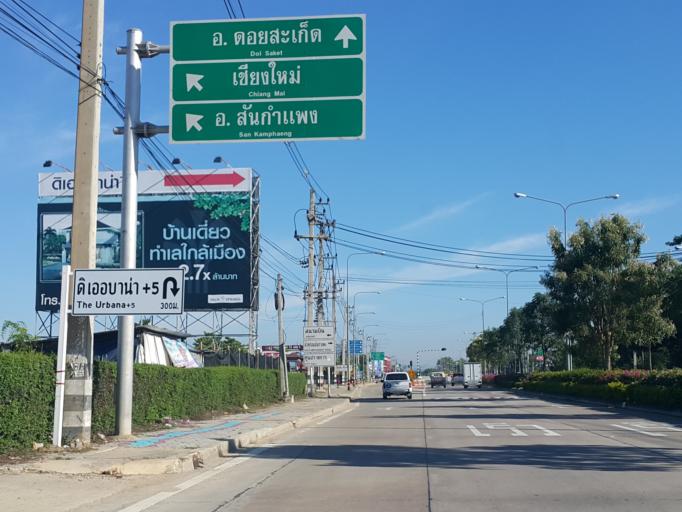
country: TH
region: Chiang Mai
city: Saraphi
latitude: 18.7596
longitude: 99.0376
